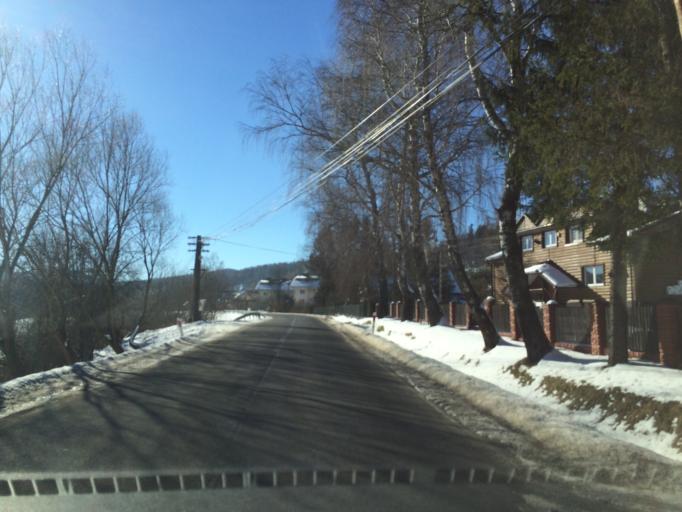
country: PL
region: Subcarpathian Voivodeship
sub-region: Powiat bieszczadzki
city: Lutowiska
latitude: 49.1902
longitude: 22.6832
